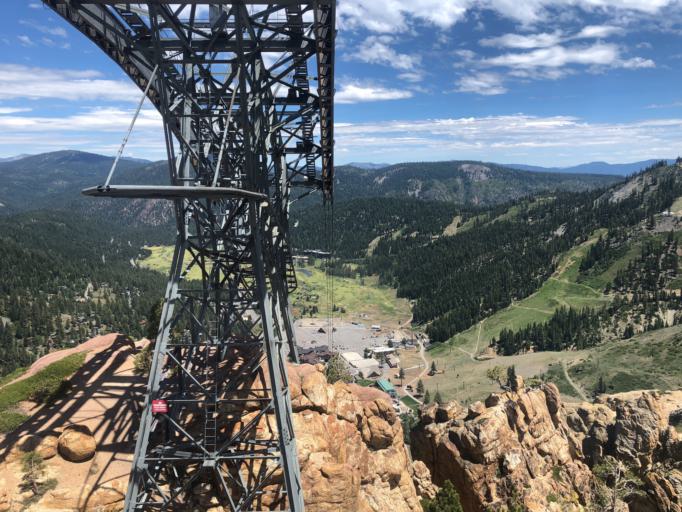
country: US
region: California
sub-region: Placer County
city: Sunnyside-Tahoe City
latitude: 39.1961
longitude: -120.2464
